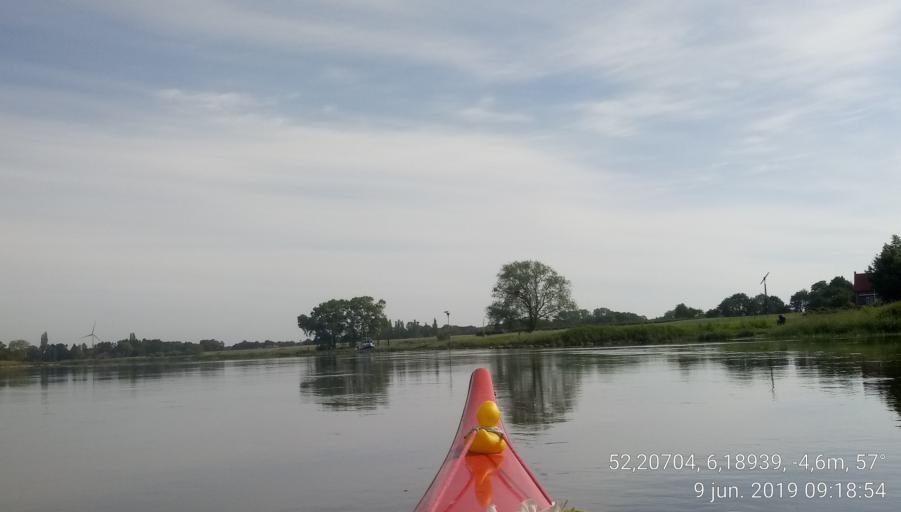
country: NL
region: Gelderland
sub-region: Gemeente Lochem
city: Gorssel
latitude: 52.2070
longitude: 6.1894
